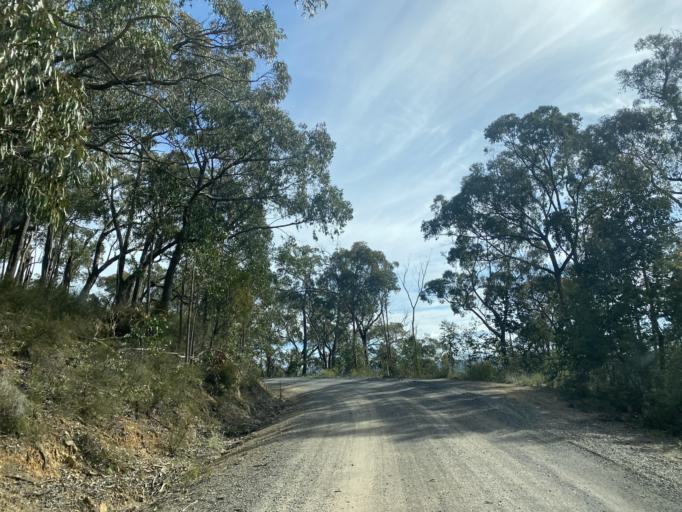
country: AU
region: Victoria
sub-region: Mansfield
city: Mansfield
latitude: -36.8436
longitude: 146.1663
